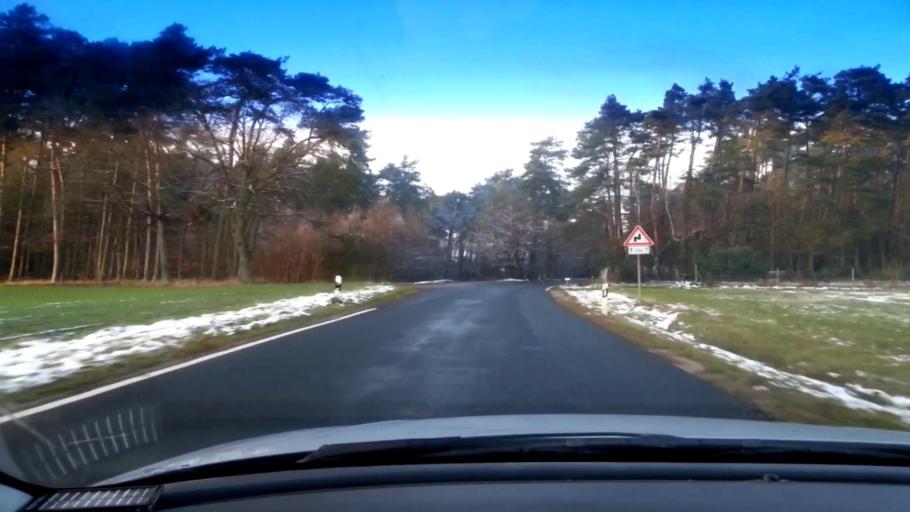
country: DE
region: Bavaria
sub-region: Regierungsbezirk Mittelfranken
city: Adelsdorf
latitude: 49.7646
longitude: 10.8941
